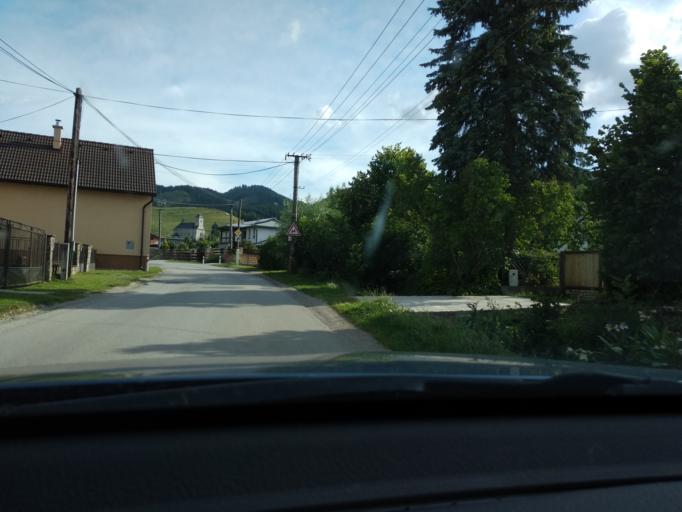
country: SK
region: Zilinsky
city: Ruzomberok
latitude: 49.0506
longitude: 19.3323
